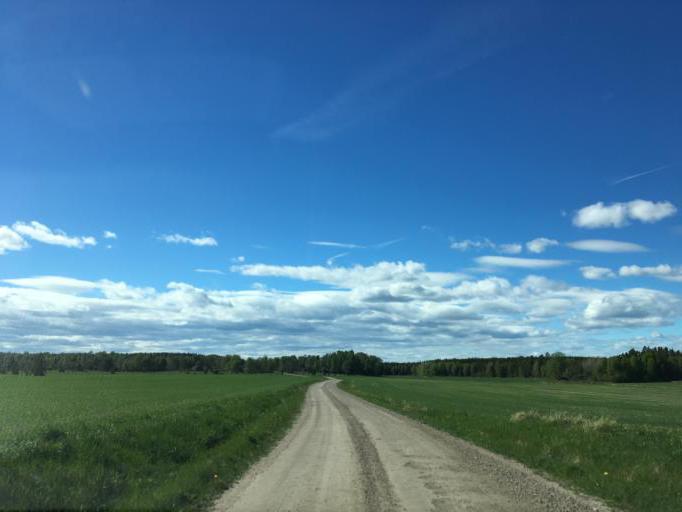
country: SE
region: Soedermanland
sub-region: Eskilstuna Kommun
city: Kvicksund
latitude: 59.3770
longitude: 16.2620
